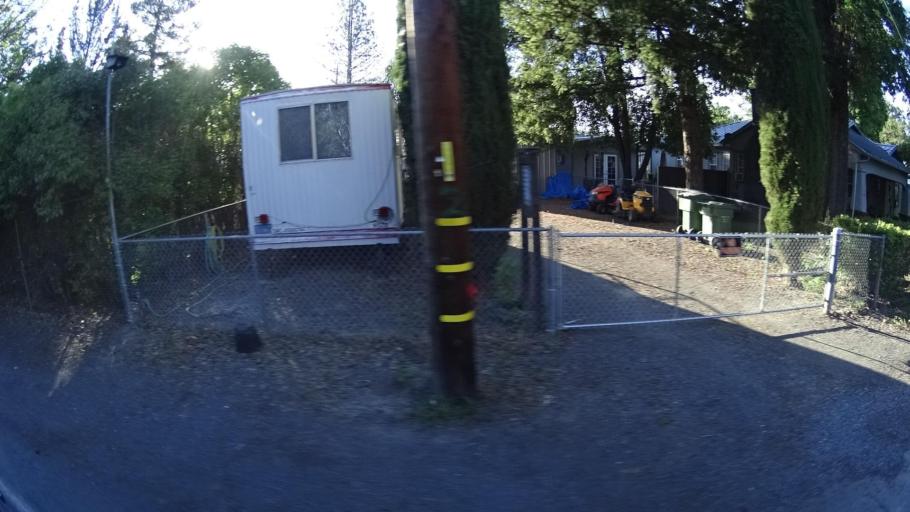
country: US
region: California
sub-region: Lake County
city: Upper Lake
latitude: 39.1668
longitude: -122.9080
